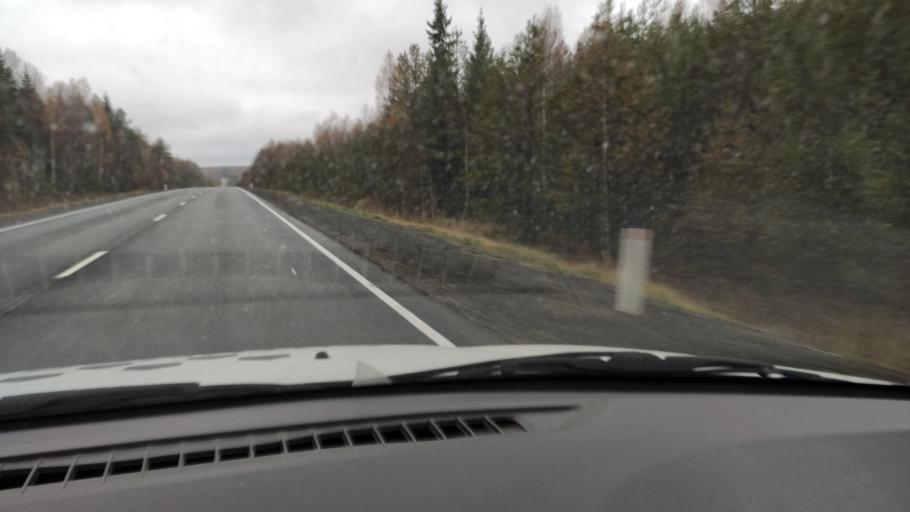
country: RU
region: Kirov
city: Chernaya Kholunitsa
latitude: 58.8873
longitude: 51.3829
